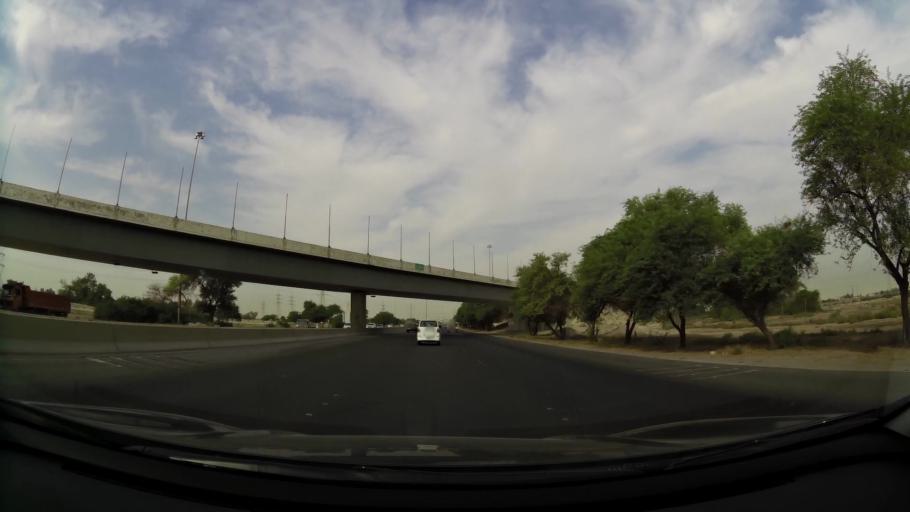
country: KW
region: Al Asimah
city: Ar Rabiyah
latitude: 29.2653
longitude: 47.8406
